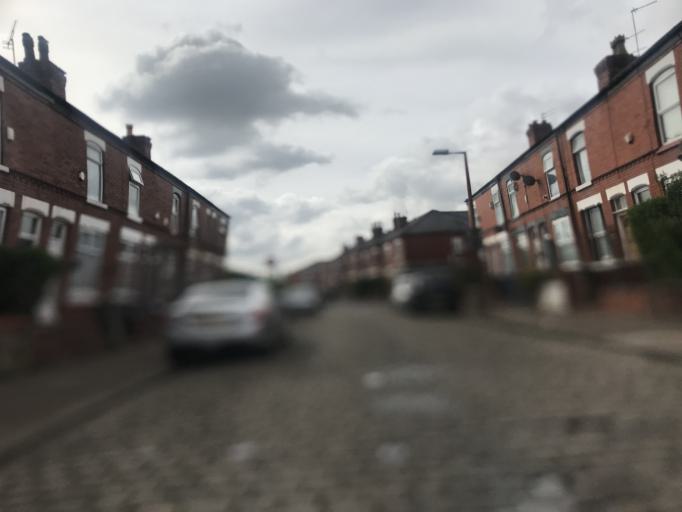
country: GB
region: England
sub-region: Borough of Stockport
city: Stockport
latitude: 53.3976
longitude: -2.1678
